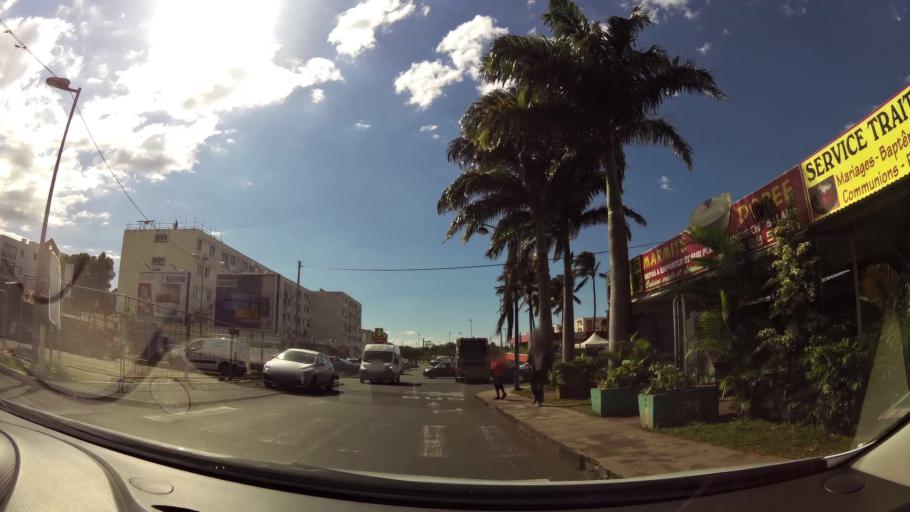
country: RE
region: Reunion
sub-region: Reunion
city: Saint-Denis
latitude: -20.8933
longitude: 55.4871
